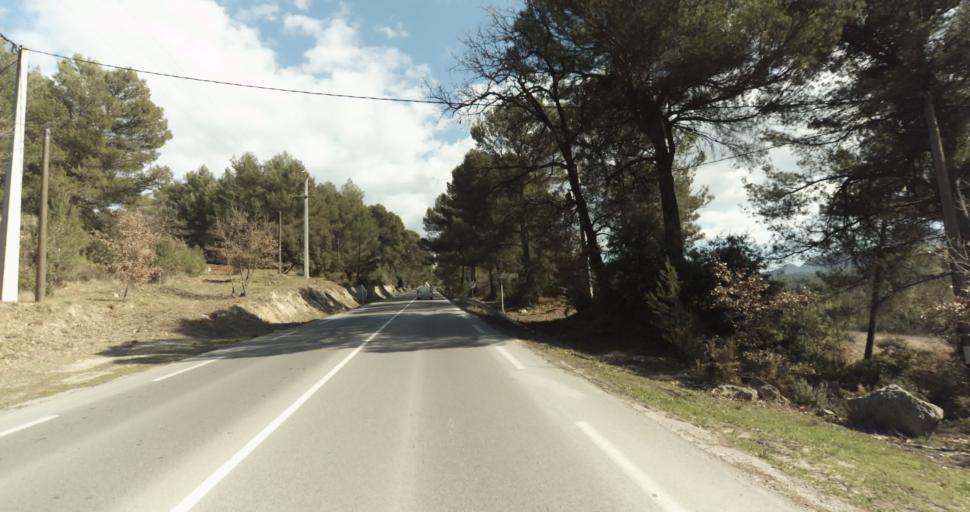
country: FR
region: Provence-Alpes-Cote d'Azur
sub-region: Departement des Bouches-du-Rhone
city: Gardanne
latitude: 43.4509
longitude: 5.4990
